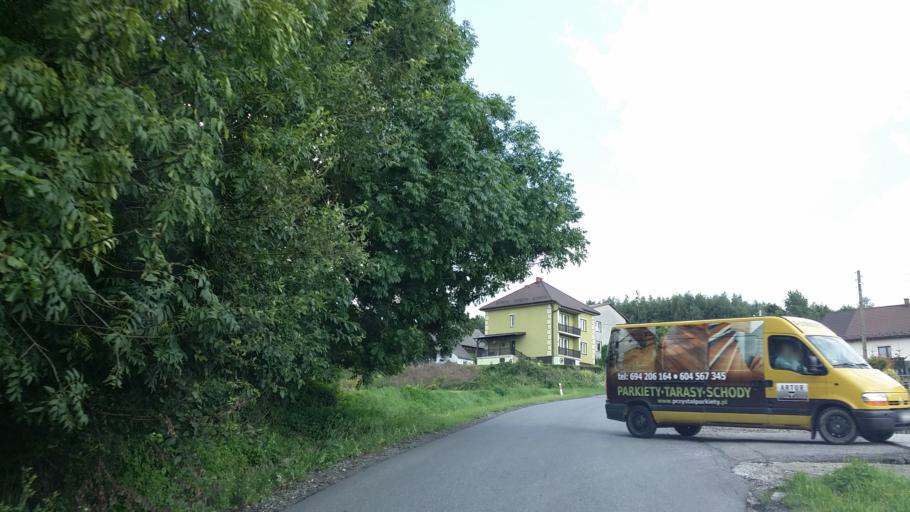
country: PL
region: Lesser Poland Voivodeship
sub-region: Powiat wadowicki
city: Spytkowice
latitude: 49.9909
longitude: 19.4759
